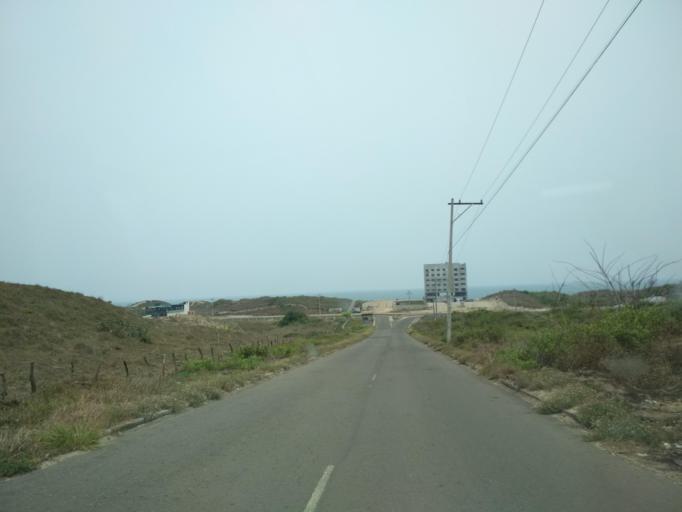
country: MX
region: Veracruz
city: Anton Lizardo
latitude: 19.0509
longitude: -96.0309
